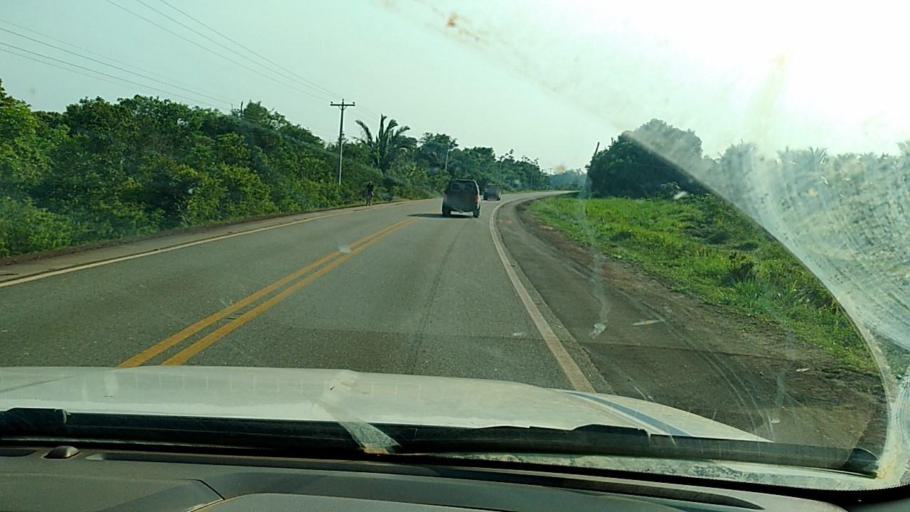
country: BR
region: Rondonia
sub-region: Porto Velho
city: Porto Velho
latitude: -8.2180
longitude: -63.9232
